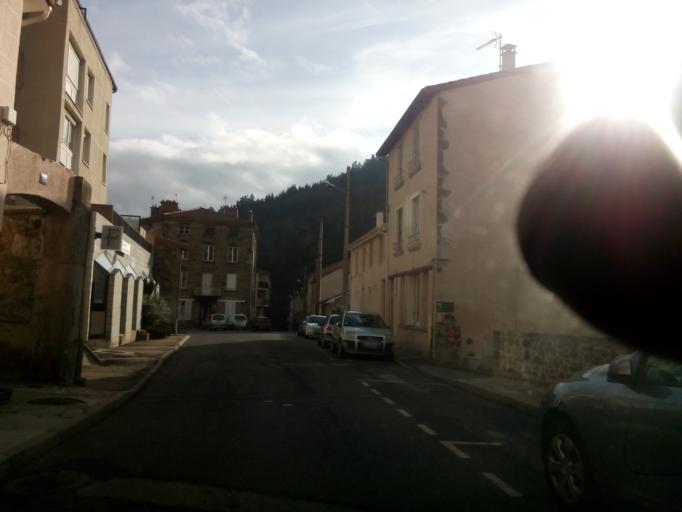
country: FR
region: Rhone-Alpes
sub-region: Departement de la Loire
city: Bourg-Argental
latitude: 45.2961
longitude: 4.5622
